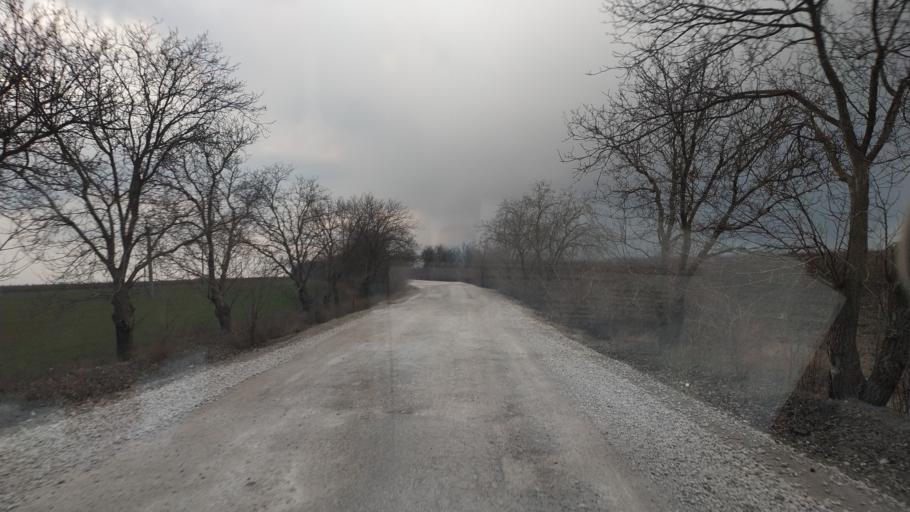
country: MD
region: Telenesti
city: Grigoriopol
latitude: 47.0412
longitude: 29.2941
